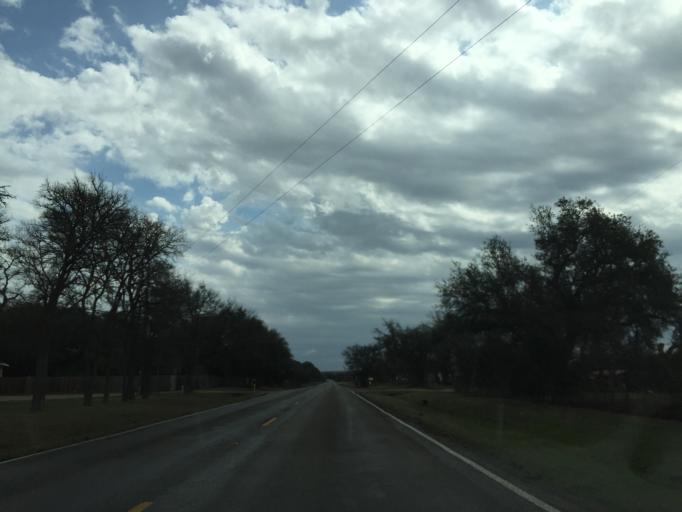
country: US
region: Texas
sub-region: Burnet County
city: Bertram
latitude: 30.6542
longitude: -97.9924
